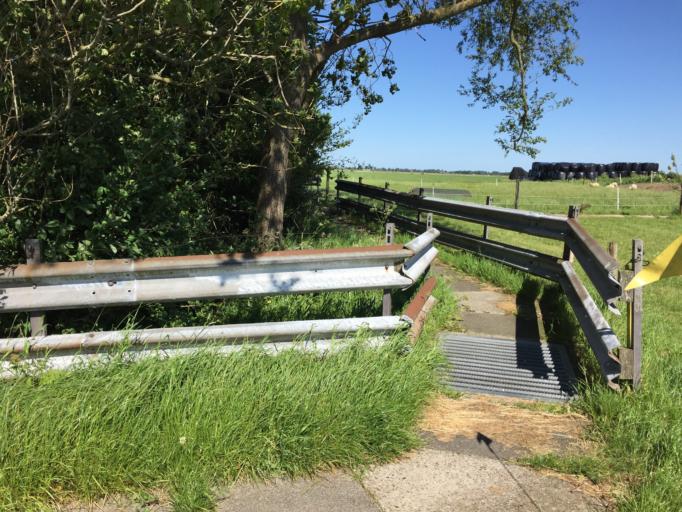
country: NL
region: Friesland
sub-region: Gemeente Boarnsterhim
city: Warten
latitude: 53.1827
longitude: 5.8802
